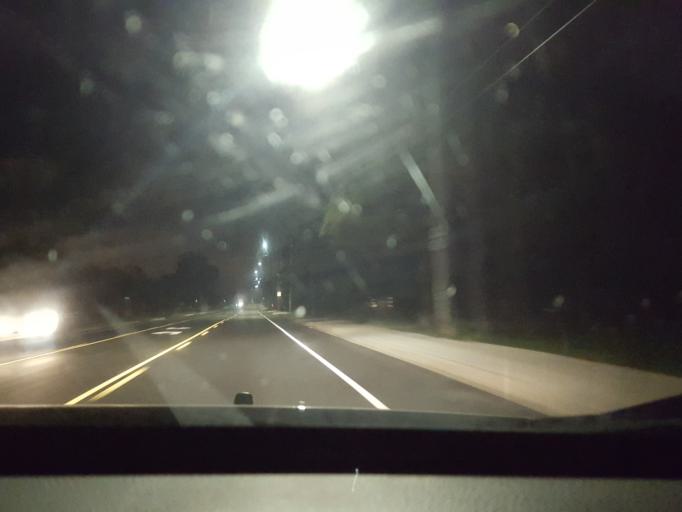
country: CA
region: Ontario
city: Hamilton
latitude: 43.2159
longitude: -79.8922
